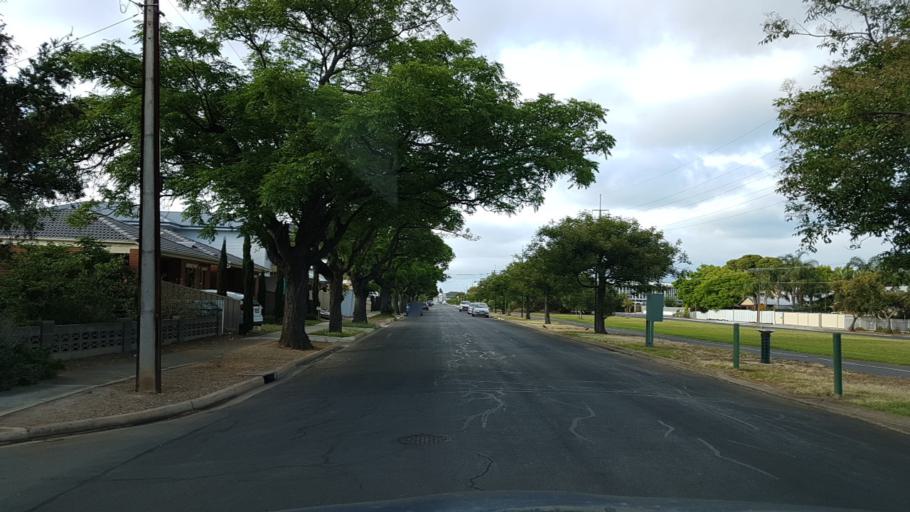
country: AU
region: South Australia
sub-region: Unley
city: Forestville
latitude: -34.9433
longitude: 138.5671
